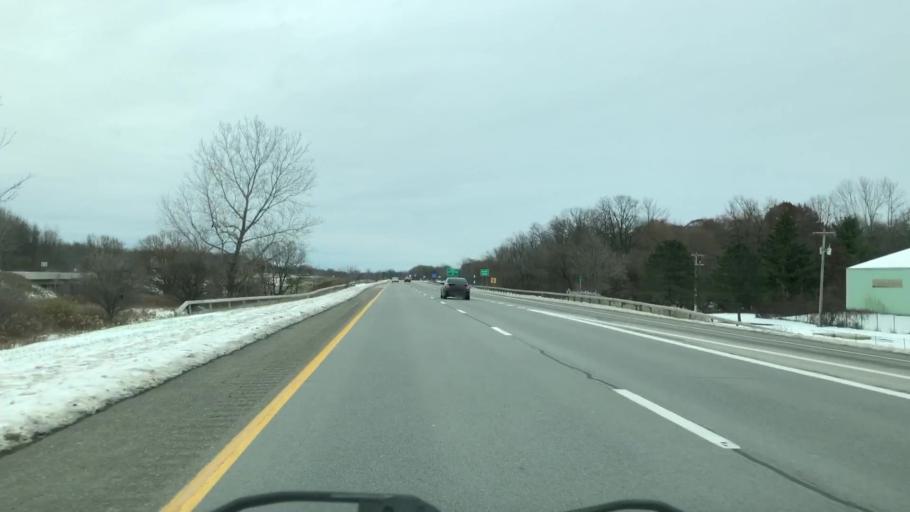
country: US
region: New York
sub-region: Monroe County
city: Churchville
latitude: 43.0938
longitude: -77.8818
